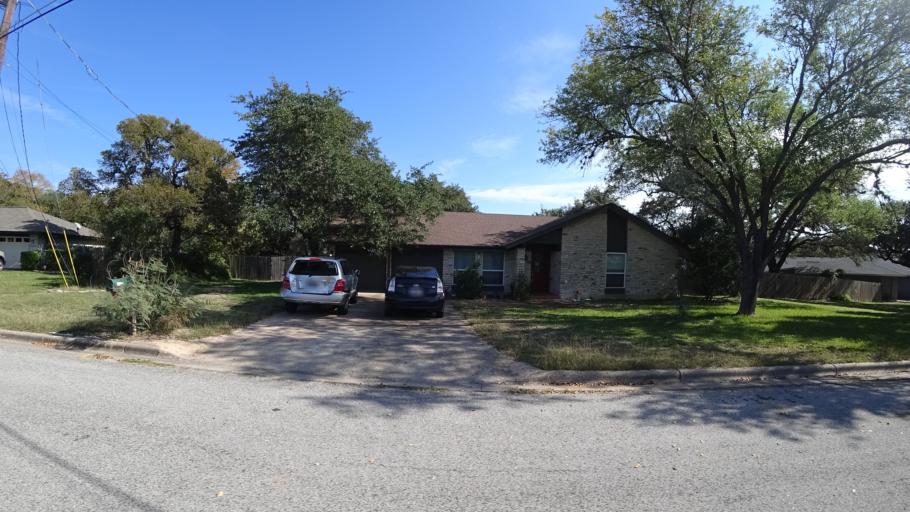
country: US
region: Texas
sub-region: Travis County
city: Shady Hollow
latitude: 30.2186
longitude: -97.9085
